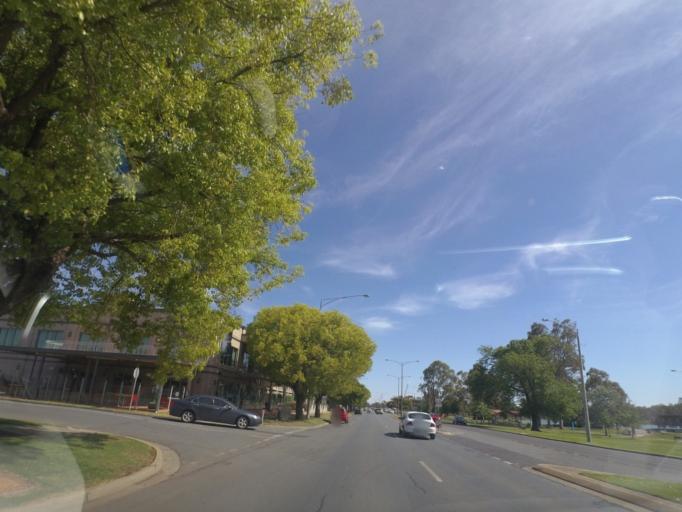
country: AU
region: Victoria
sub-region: Greater Shepparton
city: Shepparton
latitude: -36.3863
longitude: 145.3983
